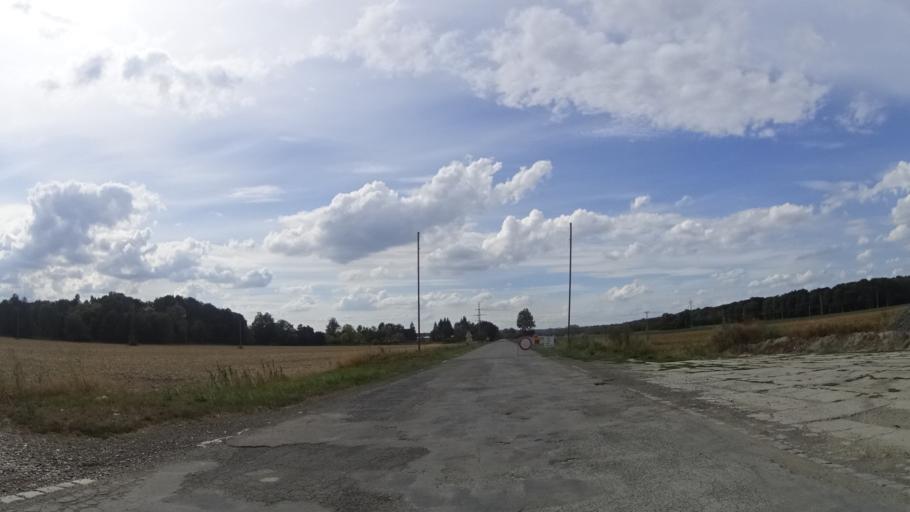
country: CZ
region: Olomoucky
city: Litovel
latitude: 49.7106
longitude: 17.0675
